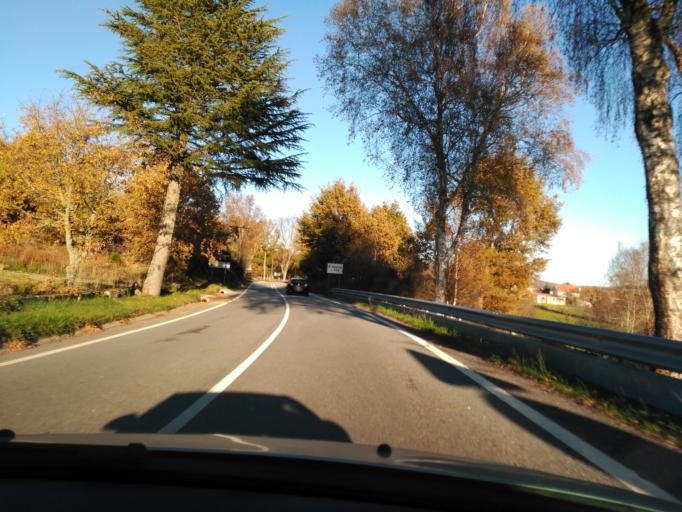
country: PT
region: Vila Real
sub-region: Montalegre
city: Montalegre
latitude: 41.7801
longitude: -7.7934
